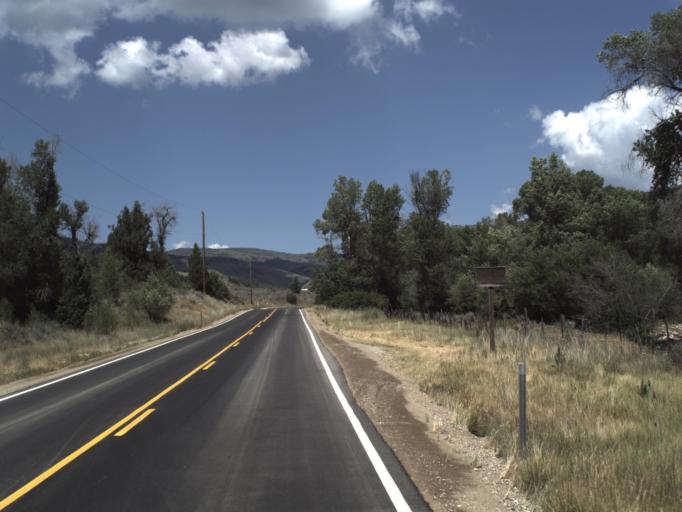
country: US
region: Utah
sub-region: Weber County
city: Wolf Creek
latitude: 41.2989
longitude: -111.6190
